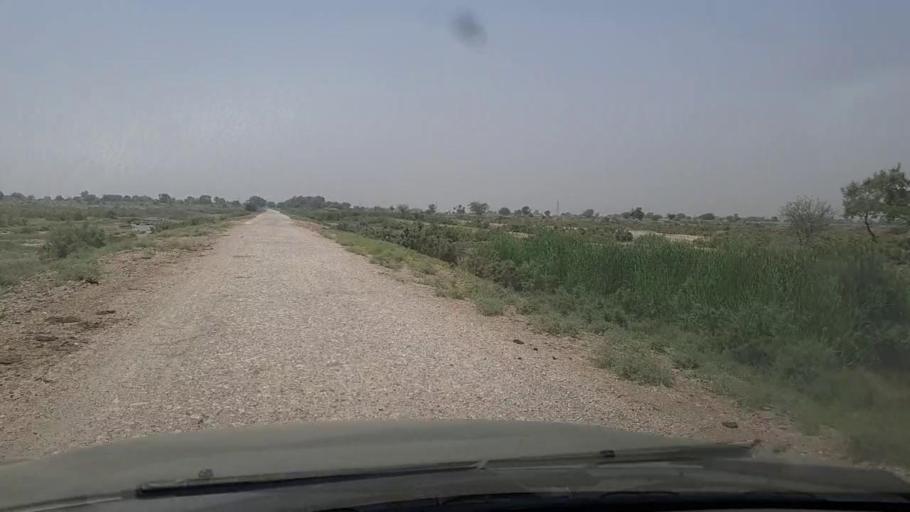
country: PK
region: Sindh
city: Ratodero
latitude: 27.7885
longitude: 68.2128
